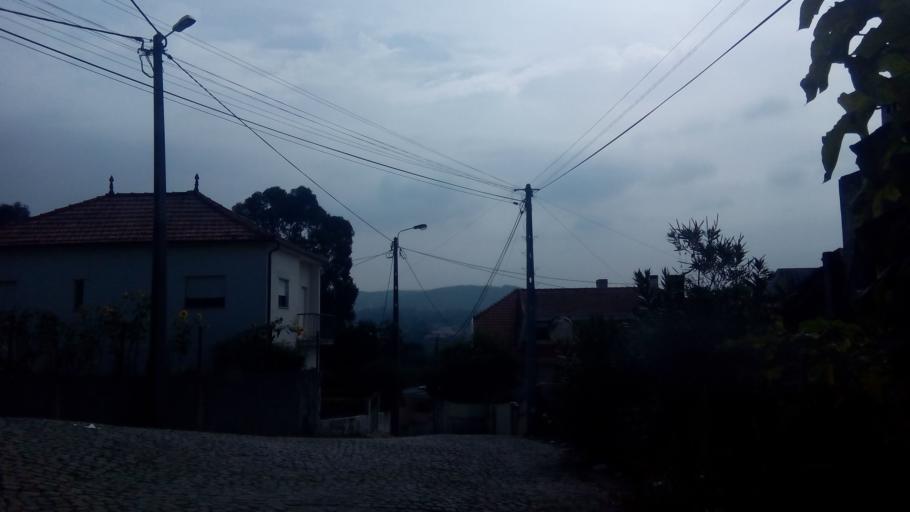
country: PT
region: Porto
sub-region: Paredes
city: Gandra
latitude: 41.1906
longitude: -8.4374
